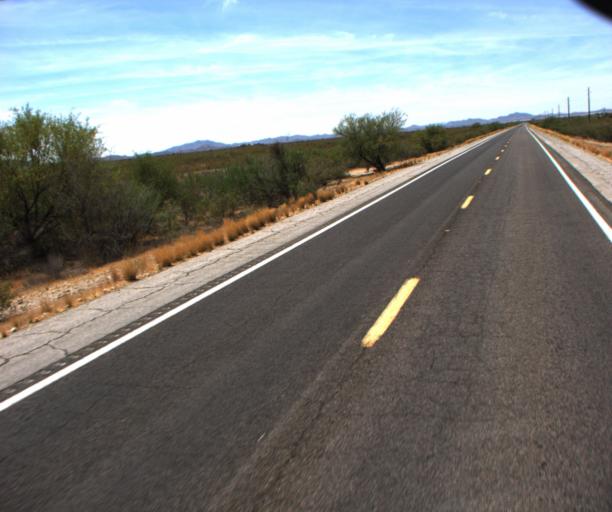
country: US
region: Arizona
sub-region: La Paz County
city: Salome
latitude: 33.8373
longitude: -113.4881
